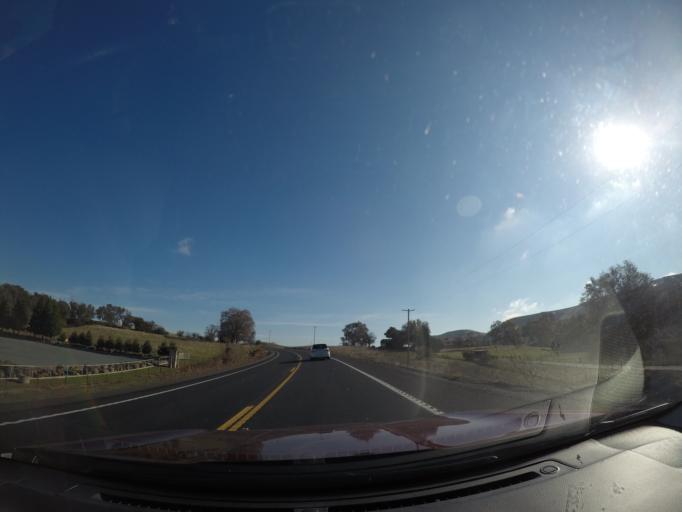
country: US
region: California
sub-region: Stanislaus County
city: East Oakdale
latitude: 37.8044
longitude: -120.6782
